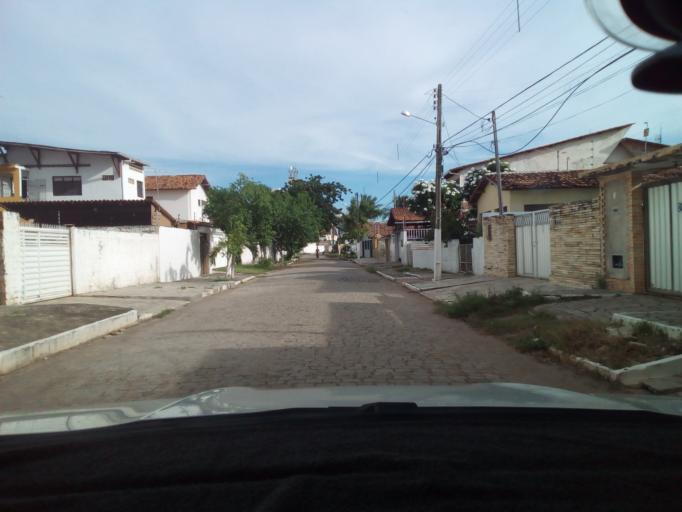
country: BR
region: Paraiba
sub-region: Cabedelo
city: Cabedelo
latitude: -7.0212
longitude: -34.8312
